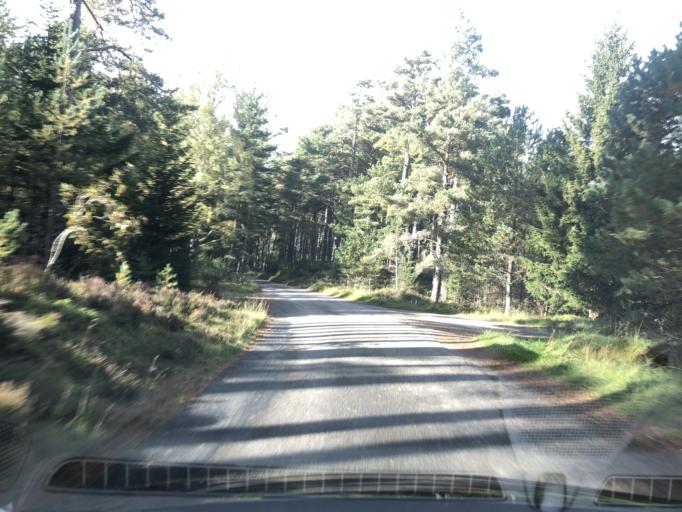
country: GB
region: Scotland
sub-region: Highland
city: Aviemore
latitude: 57.1159
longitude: -3.8954
